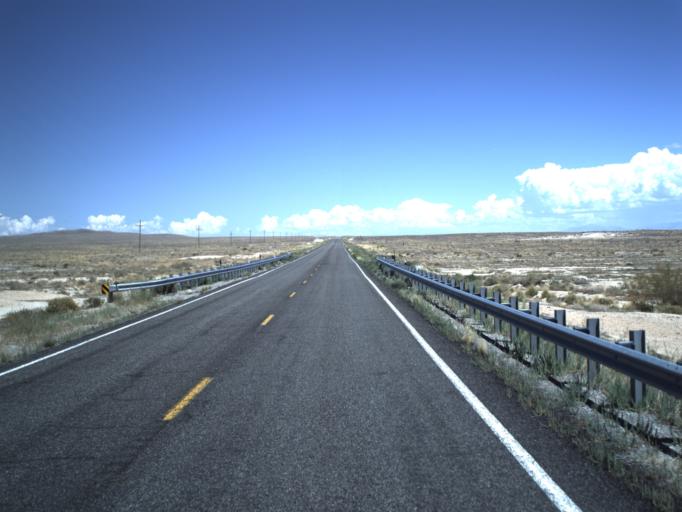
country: US
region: Utah
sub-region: Millard County
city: Delta
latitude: 39.1172
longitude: -113.1258
